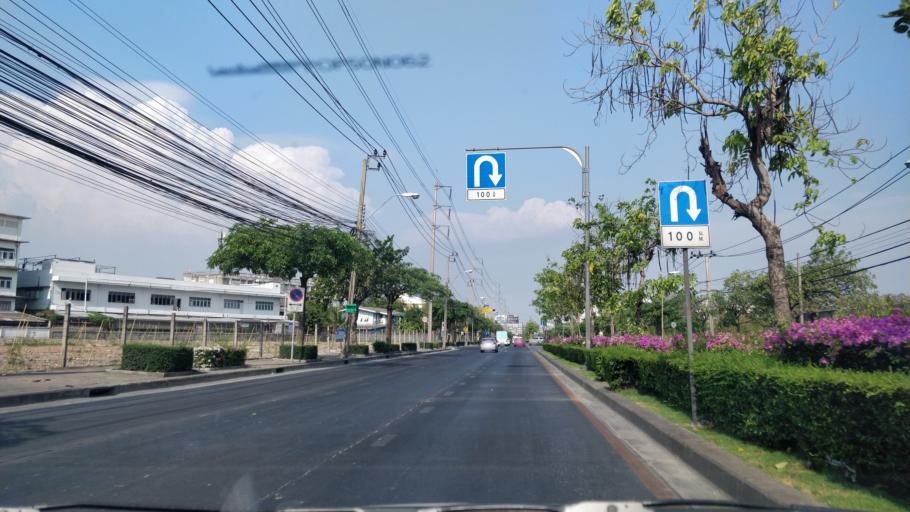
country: TH
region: Bangkok
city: Suan Luang
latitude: 13.7194
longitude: 100.6727
